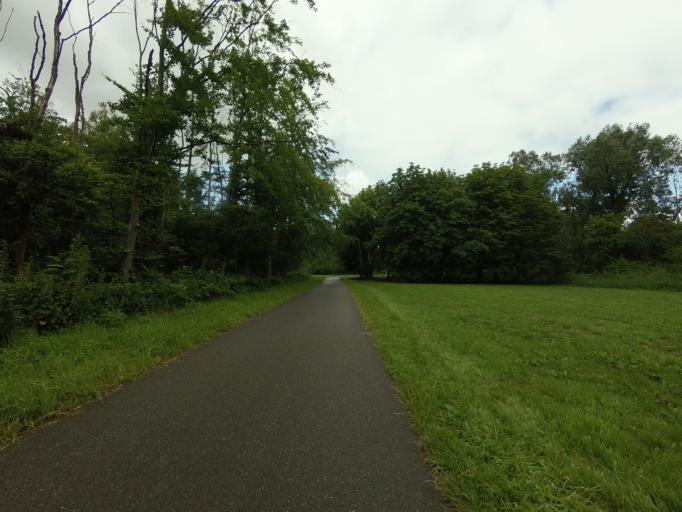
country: NL
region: North Holland
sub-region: Gemeente Velsen
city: Velsen-Zuid
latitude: 52.4413
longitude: 4.6904
